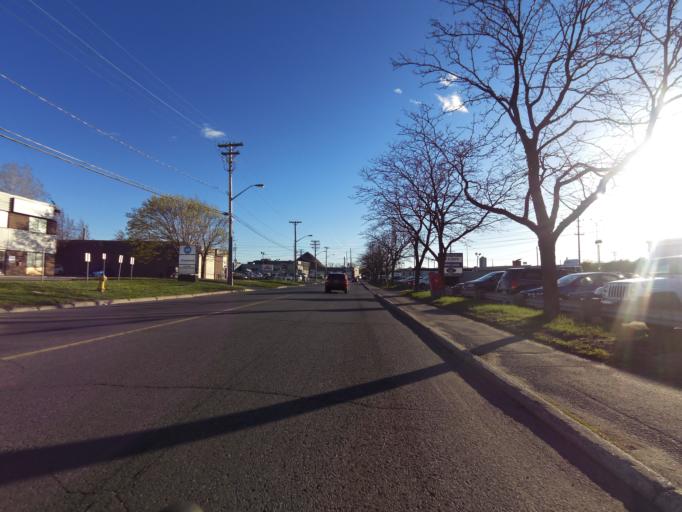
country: CA
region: Ontario
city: Ottawa
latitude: 45.3762
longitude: -75.7464
